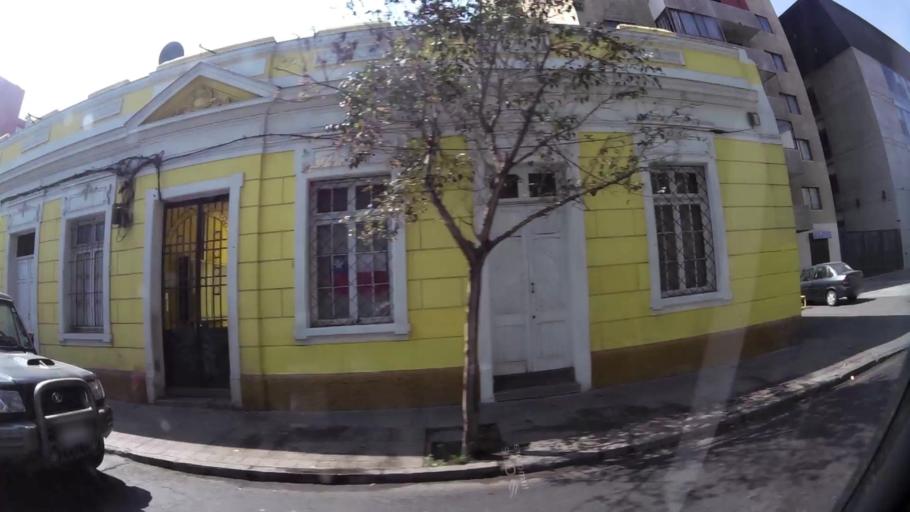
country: CL
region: Santiago Metropolitan
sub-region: Provincia de Santiago
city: Santiago
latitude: -33.4513
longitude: -70.6562
